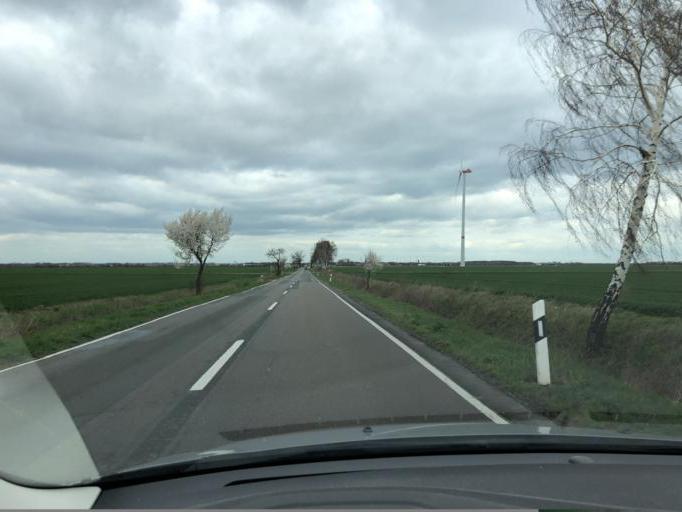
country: DE
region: Saxony-Anhalt
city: Lutzen
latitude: 51.2279
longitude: 12.1395
